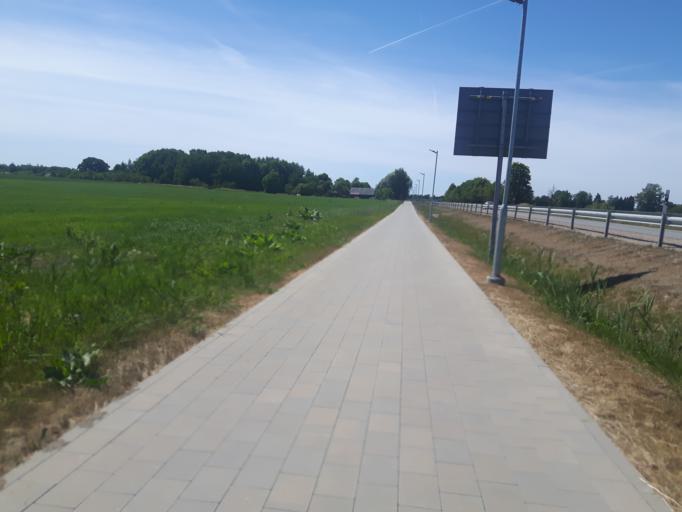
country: LV
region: Grobina
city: Grobina
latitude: 56.5334
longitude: 21.1237
